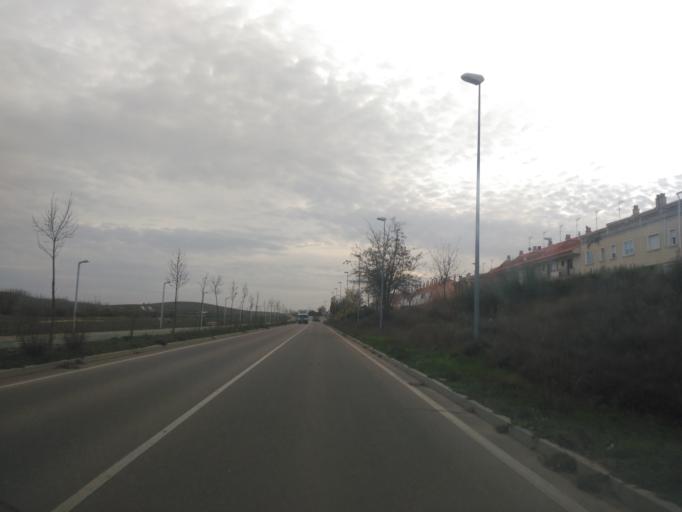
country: ES
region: Castille and Leon
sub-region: Provincia de Salamanca
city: Salamanca
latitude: 40.9515
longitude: -5.6770
